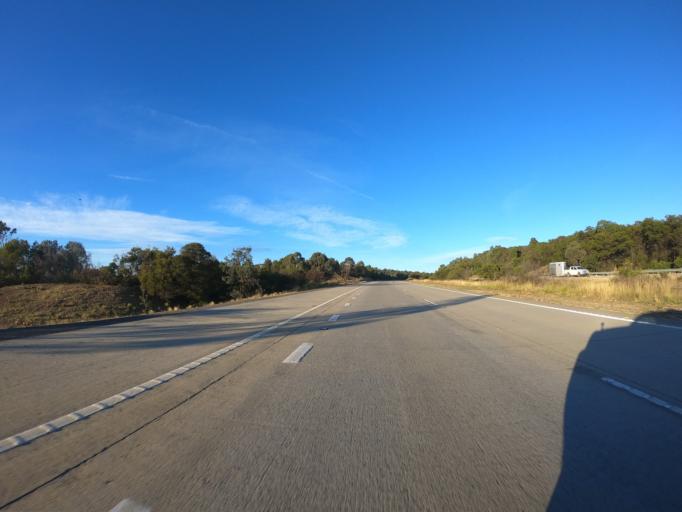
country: AU
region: New South Wales
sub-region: Yass Valley
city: Gundaroo
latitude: -35.1055
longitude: 149.3723
